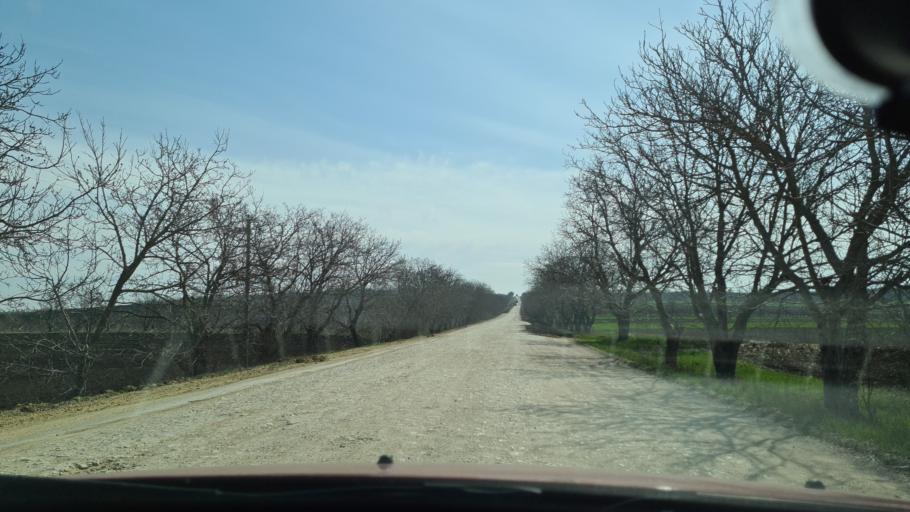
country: MD
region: Ungheni
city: Ungheni
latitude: 47.2678
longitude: 27.9532
